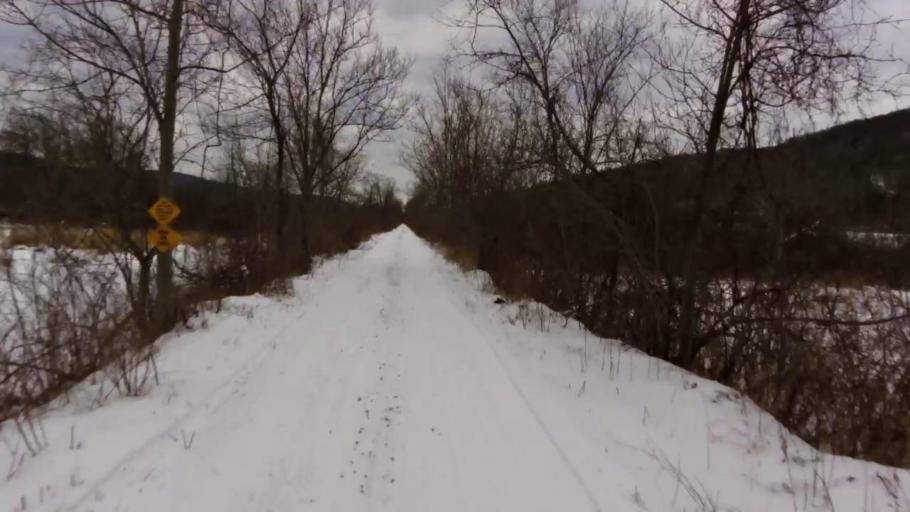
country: US
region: Pennsylvania
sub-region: McKean County
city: Foster Brook
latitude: 42.0046
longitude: -78.6230
